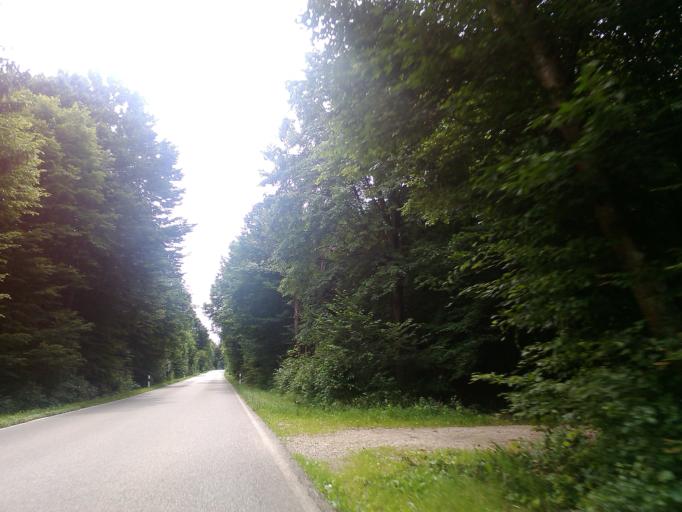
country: DE
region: Bavaria
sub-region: Upper Bavaria
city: Gauting
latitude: 48.0791
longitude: 11.3539
